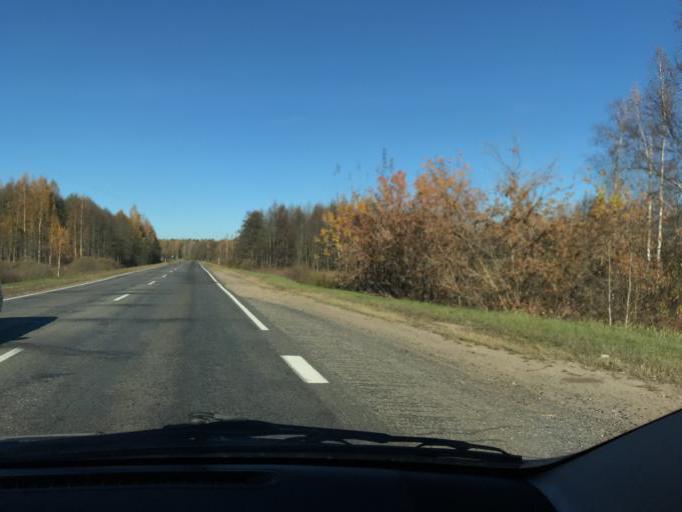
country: BY
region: Vitebsk
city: Polatsk
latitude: 55.3977
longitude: 28.8098
